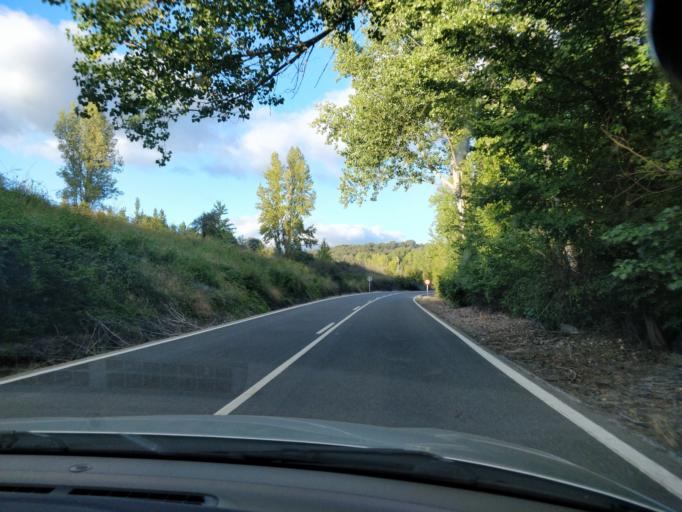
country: ES
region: Castille and Leon
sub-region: Provincia de Leon
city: Borrenes
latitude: 42.4987
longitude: -6.7327
